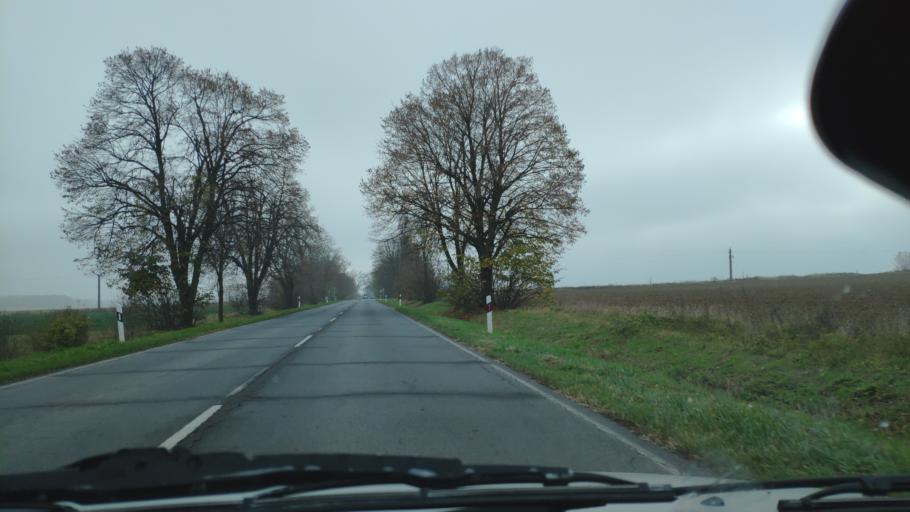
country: HU
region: Zala
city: Zalakomar
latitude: 46.5671
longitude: 17.2619
